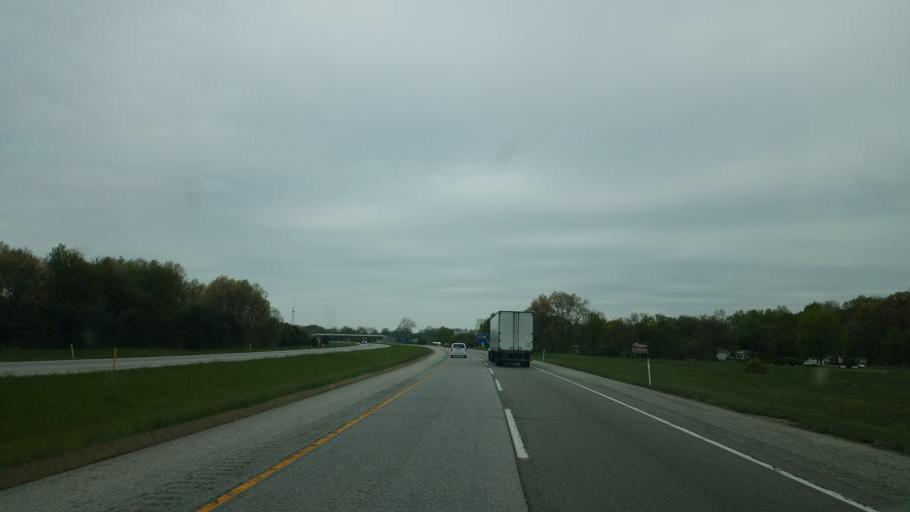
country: US
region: Michigan
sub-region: Saint Joseph County
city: White Pigeon
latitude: 41.7542
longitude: -85.6427
